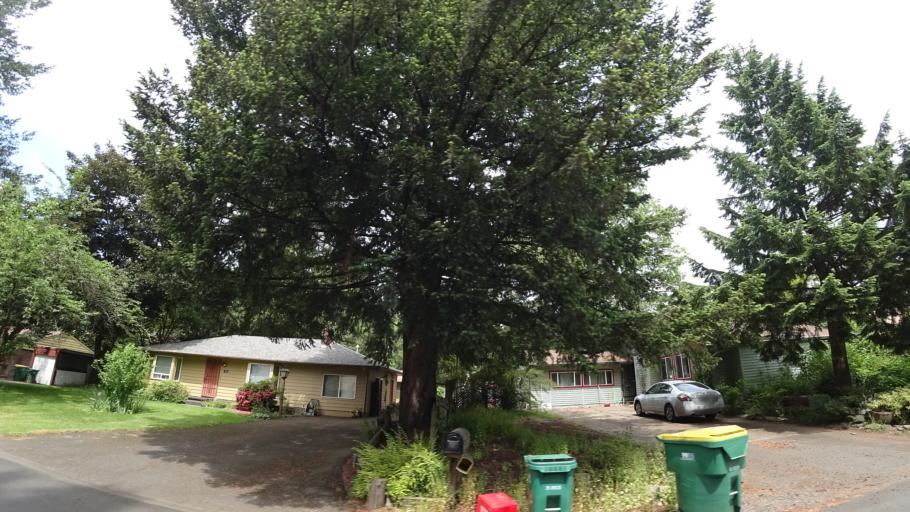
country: US
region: Oregon
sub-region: Washington County
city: Garden Home-Whitford
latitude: 45.4603
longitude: -122.7540
